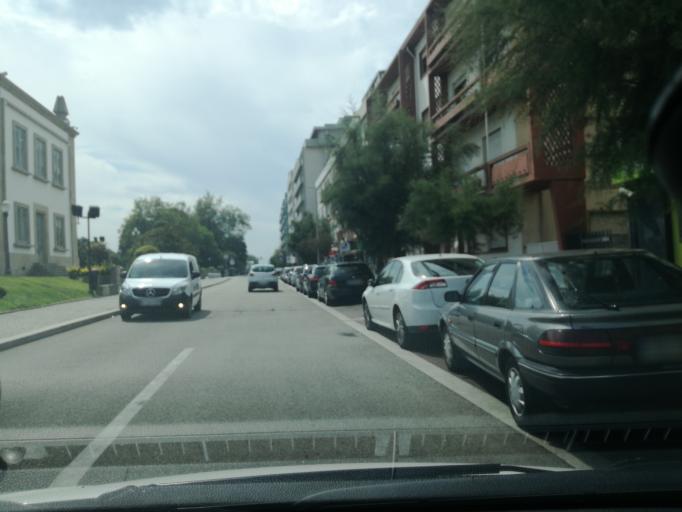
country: PT
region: Aveiro
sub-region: Espinho
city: Espinho
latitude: 41.0093
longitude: -8.6398
